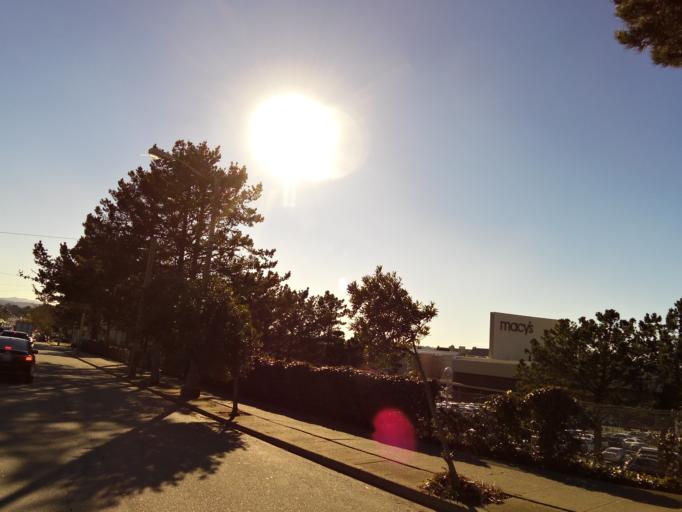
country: US
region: California
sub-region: San Mateo County
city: Daly City
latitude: 37.7298
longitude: -122.4749
